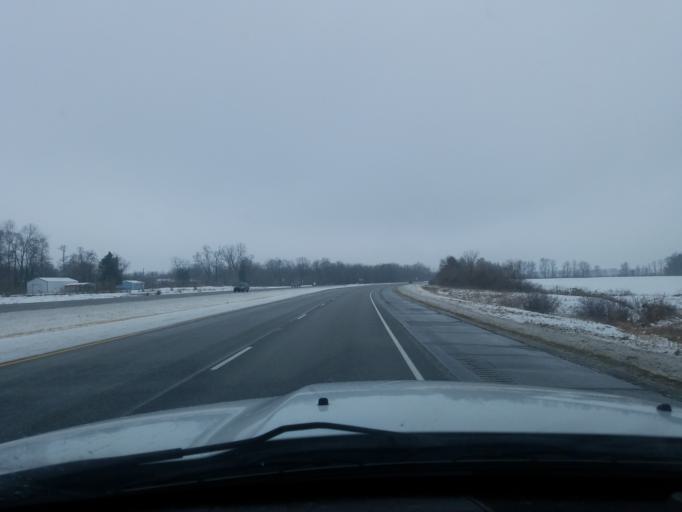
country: US
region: Indiana
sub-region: Fulton County
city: Rochester
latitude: 40.9311
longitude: -86.1671
